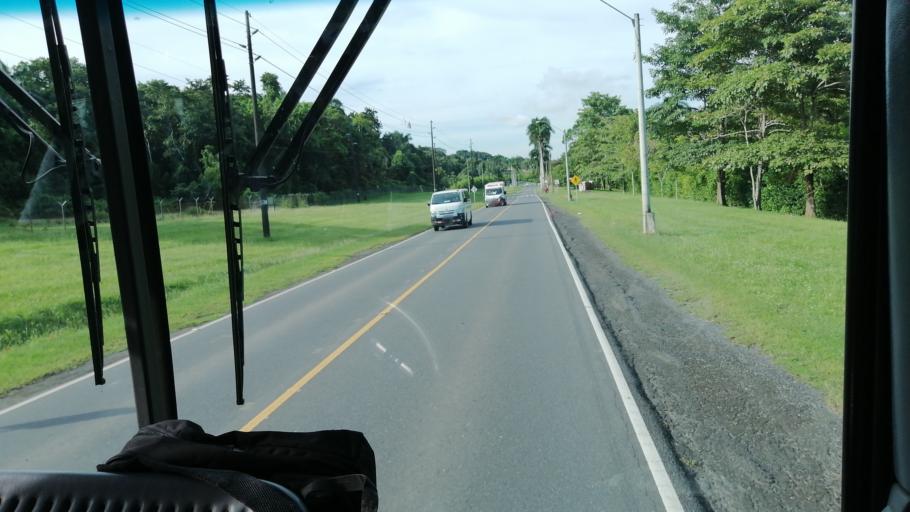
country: PA
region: Panama
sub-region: Distrito de Panama
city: Ancon
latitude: 8.9364
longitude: -79.5909
